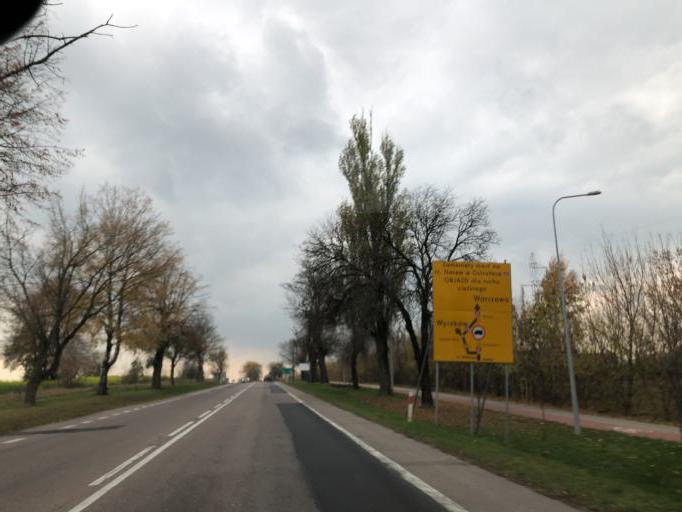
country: PL
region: Podlasie
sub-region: Lomza
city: Lomza
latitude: 53.1738
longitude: 22.0290
